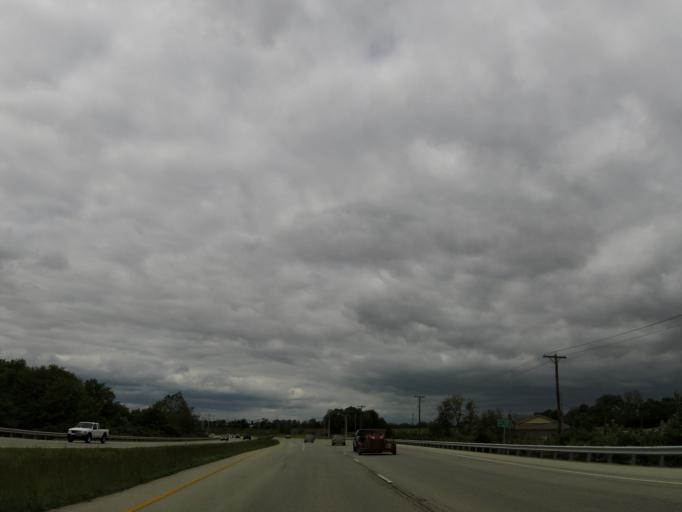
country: US
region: Kentucky
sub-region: Scott County
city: Georgetown
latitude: 38.2026
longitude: -84.5377
